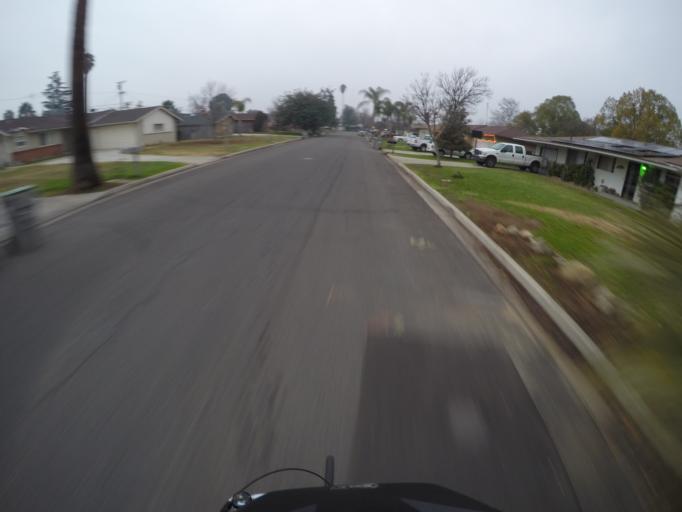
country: US
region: California
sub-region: Fresno County
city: Tarpey Village
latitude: 36.7946
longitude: -119.6975
